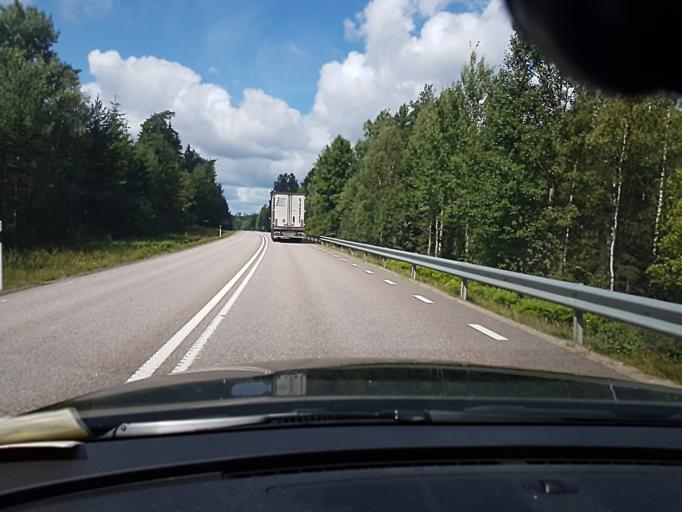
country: SE
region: Kronoberg
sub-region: Lessebo Kommun
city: Lessebo
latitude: 56.7803
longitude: 15.2427
